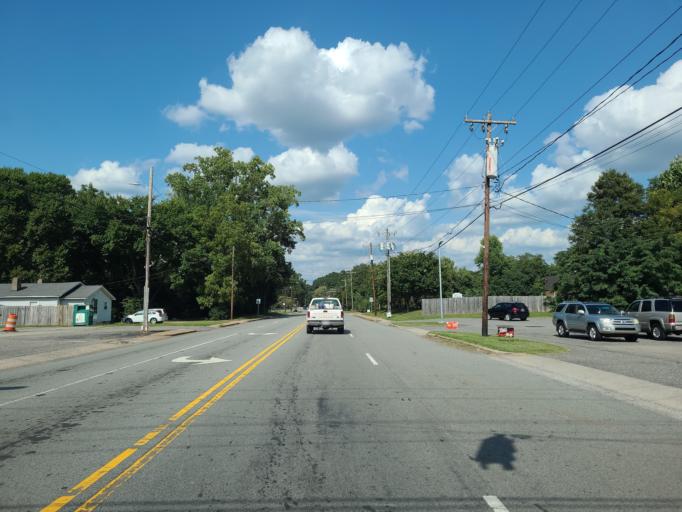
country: US
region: North Carolina
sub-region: Gaston County
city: Lowell
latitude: 35.2680
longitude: -81.0994
